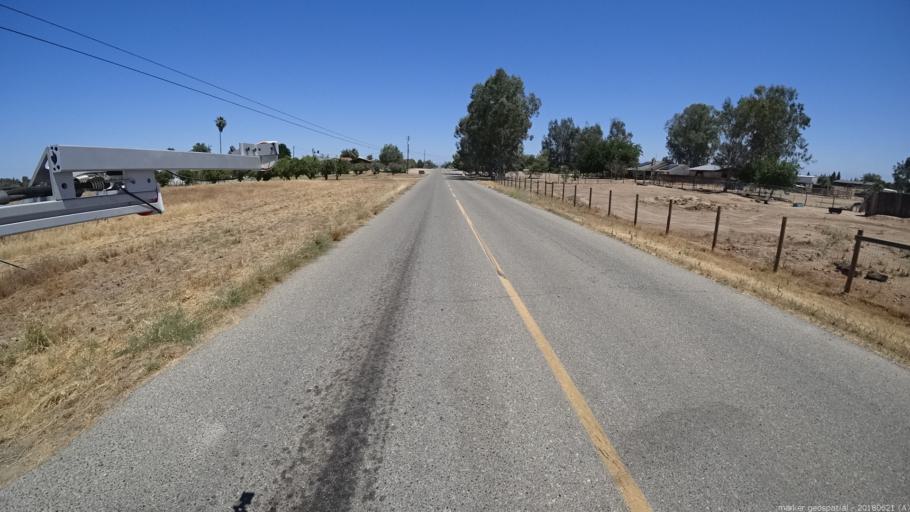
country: US
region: California
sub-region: Madera County
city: Bonadelle Ranchos-Madera Ranchos
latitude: 36.9887
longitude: -119.8758
